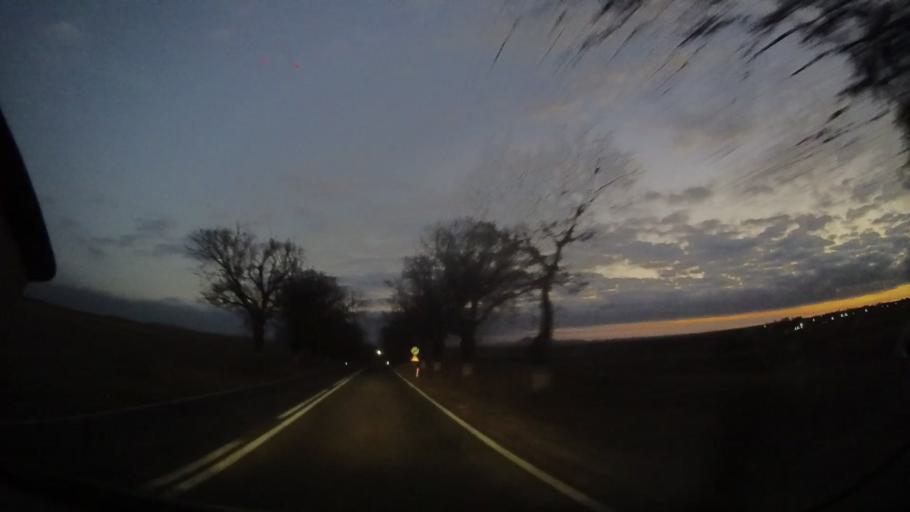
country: RO
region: Tulcea
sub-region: Comuna Frecatei
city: Cataloi
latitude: 45.0925
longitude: 28.7413
